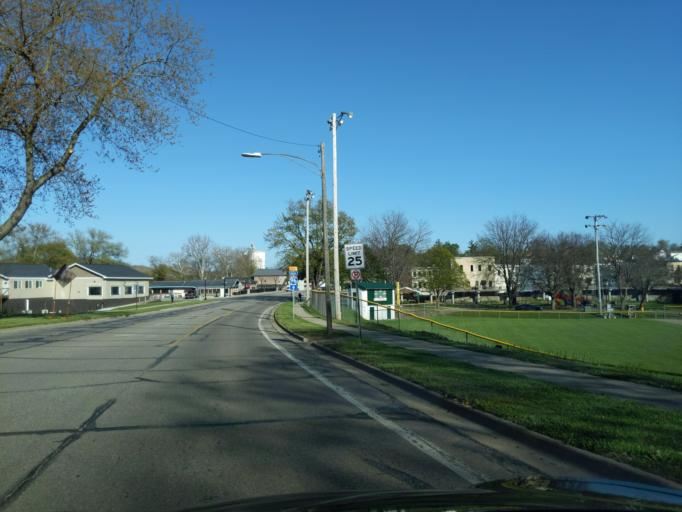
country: US
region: Michigan
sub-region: Ionia County
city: Portland
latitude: 42.8714
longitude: -84.9051
